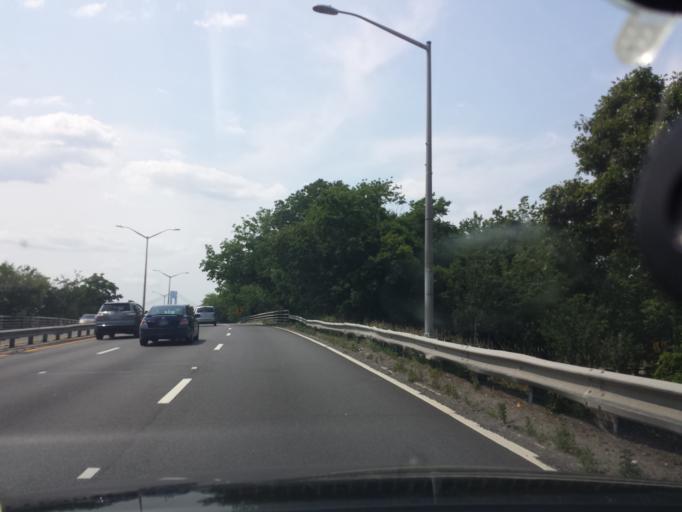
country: US
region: New York
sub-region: Kings County
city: Bensonhurst
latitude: 40.5958
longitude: -73.9993
